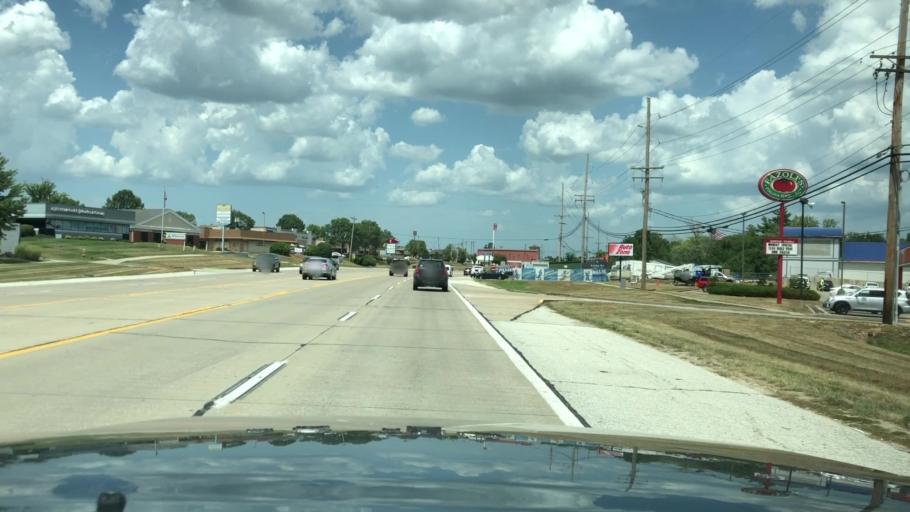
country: US
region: Missouri
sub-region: Saint Charles County
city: O'Fallon
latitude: 38.7956
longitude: -90.6996
